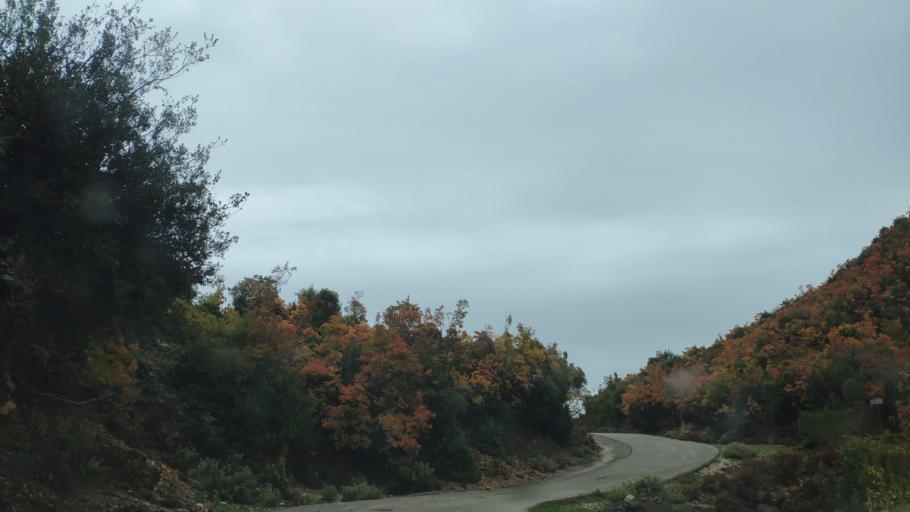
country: GR
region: Epirus
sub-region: Nomos Prevezis
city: Kanalaki
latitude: 39.3383
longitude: 20.6535
